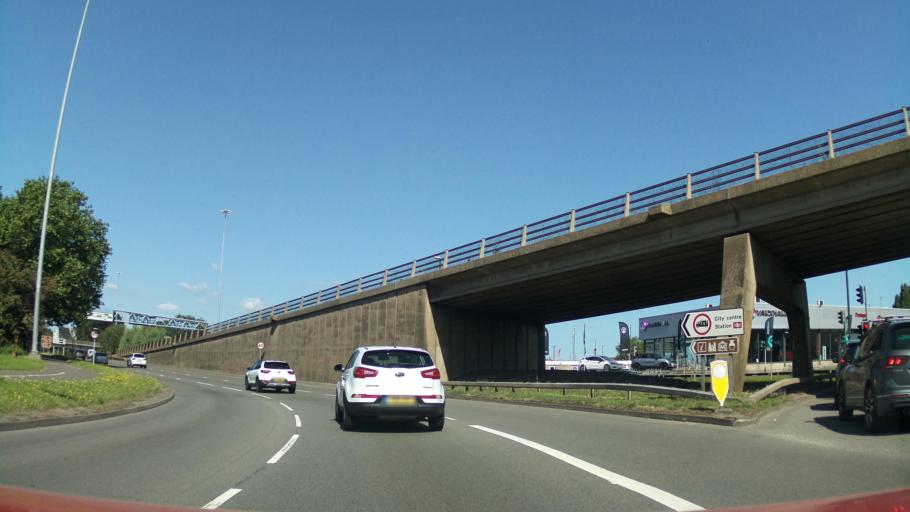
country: GB
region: England
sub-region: Derby
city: Derby
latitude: 52.9245
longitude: -1.4628
